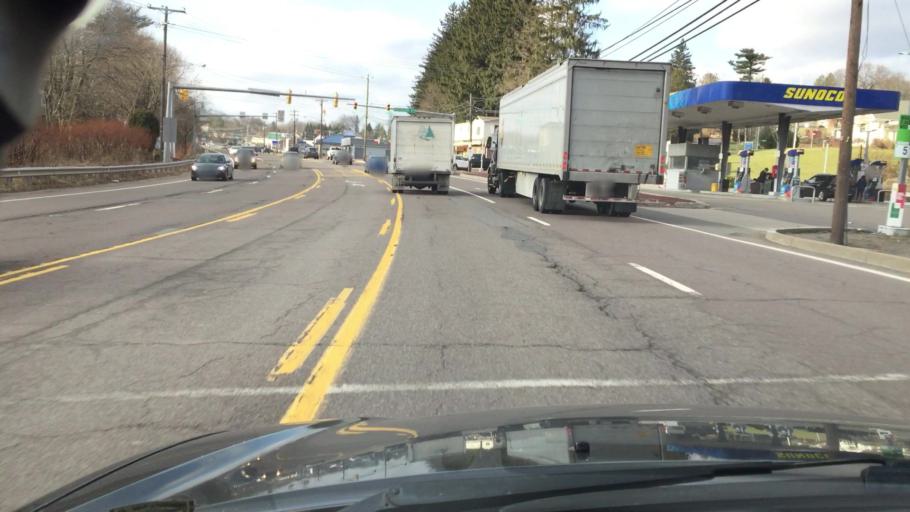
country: US
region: Pennsylvania
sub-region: Luzerne County
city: Shavertown
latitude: 41.3299
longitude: -75.9491
